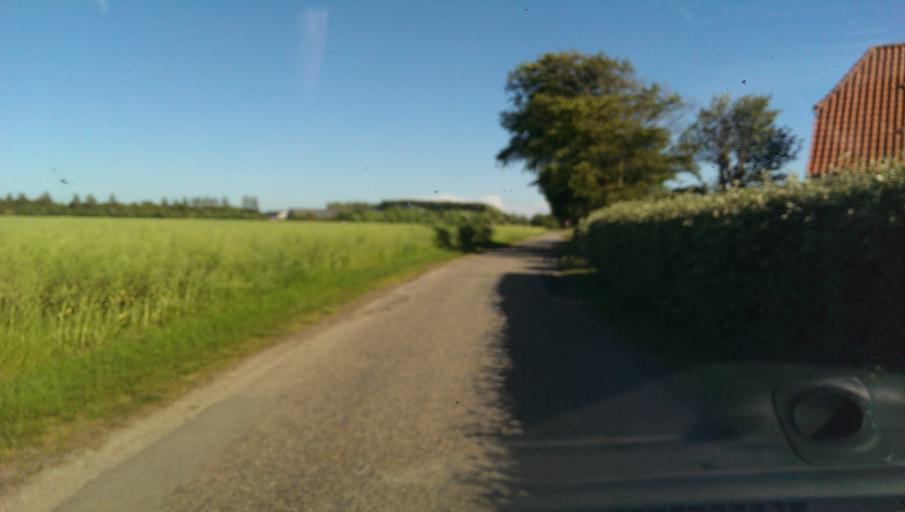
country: DK
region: South Denmark
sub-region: Fano Kommune
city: Nordby
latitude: 55.5234
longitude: 8.3912
